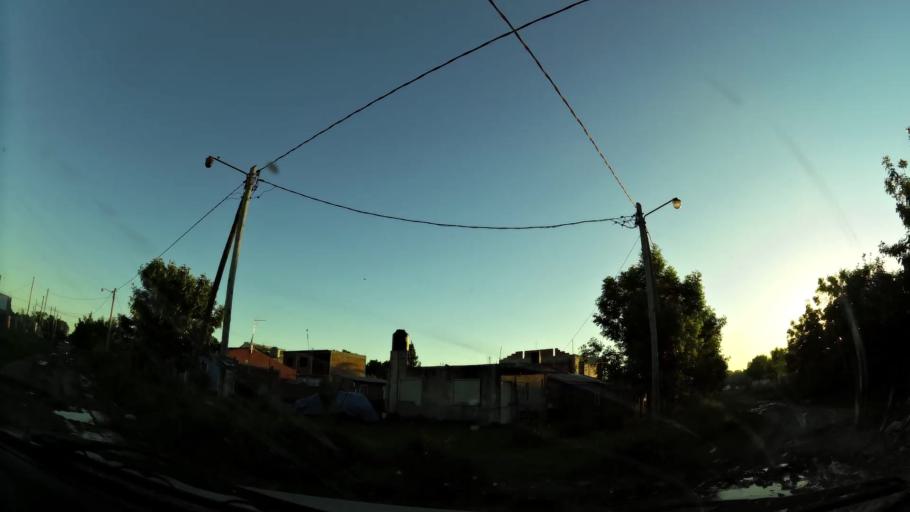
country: AR
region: Buenos Aires
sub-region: Partido de Almirante Brown
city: Adrogue
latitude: -34.7921
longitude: -58.3418
